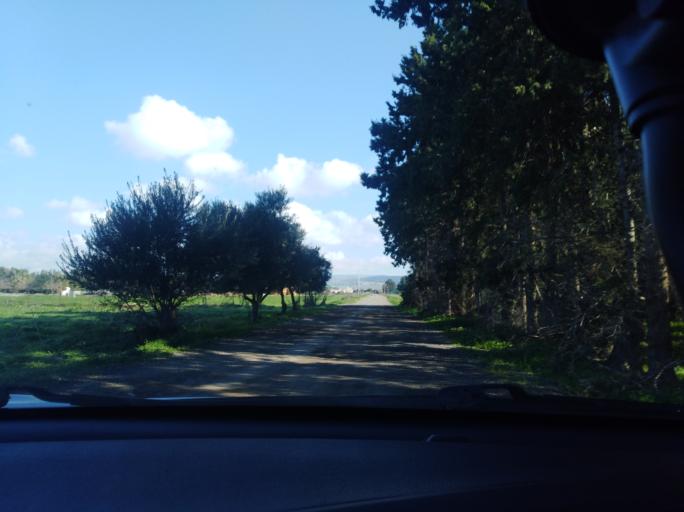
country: CY
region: Pafos
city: Paphos
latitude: 34.7383
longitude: 32.4449
